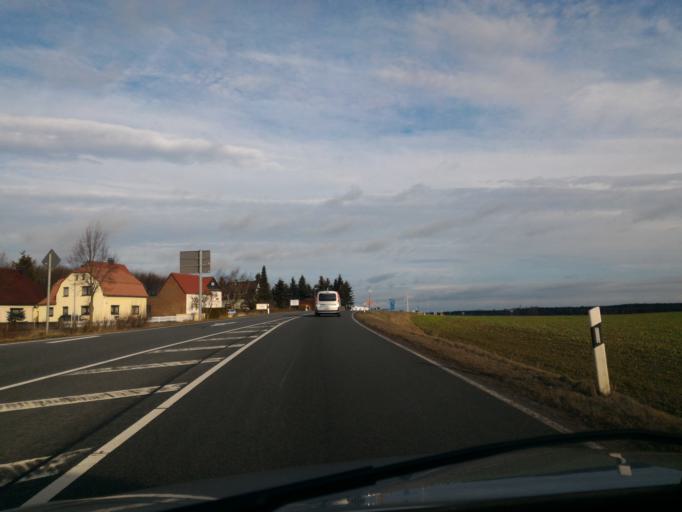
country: DE
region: Saxony
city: Neugersdorf
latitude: 50.9940
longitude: 14.6164
